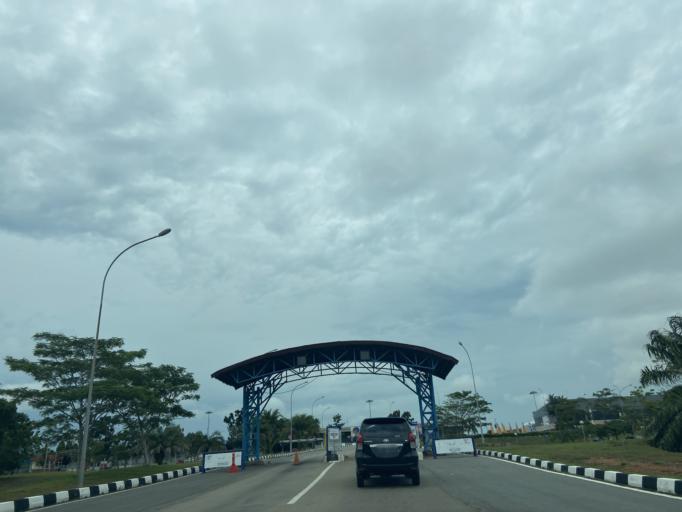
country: SG
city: Singapore
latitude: 1.1263
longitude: 104.1156
